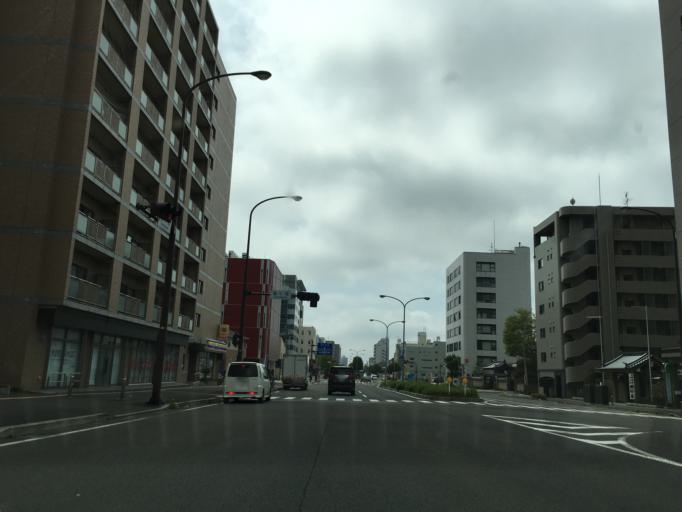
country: JP
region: Miyagi
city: Sendai-shi
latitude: 38.2607
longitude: 140.8921
